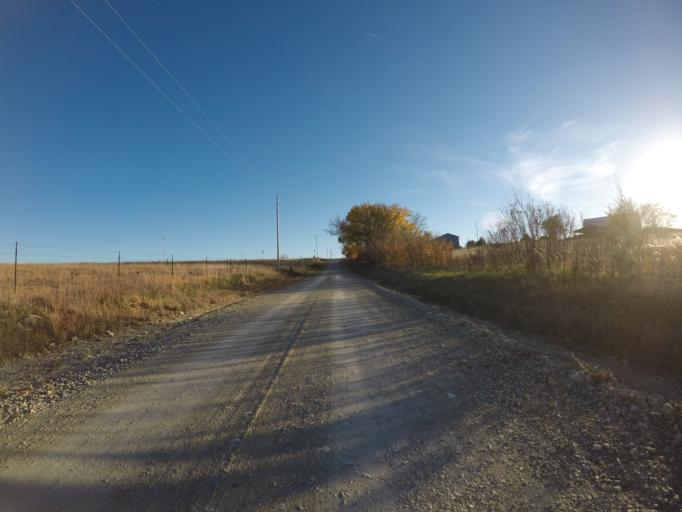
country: US
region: Kansas
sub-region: Riley County
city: Manhattan
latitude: 39.2659
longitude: -96.6817
